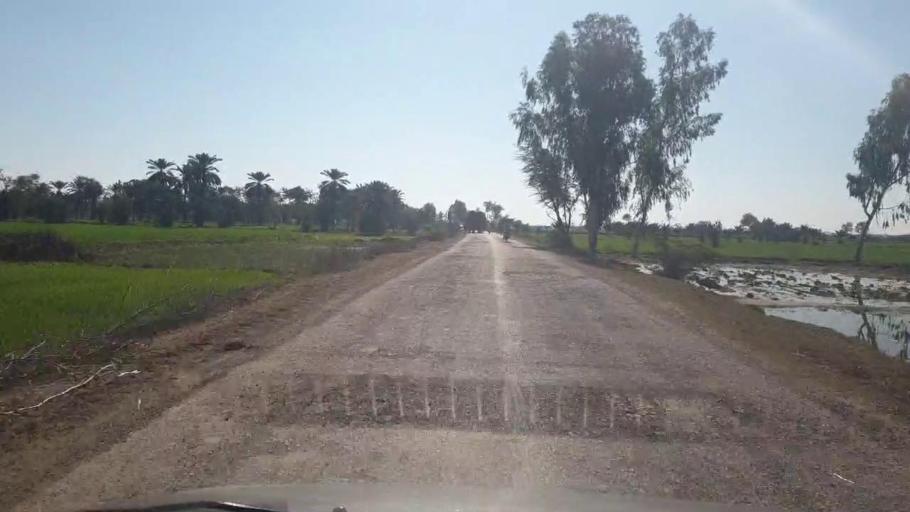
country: PK
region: Sindh
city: Bozdar
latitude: 27.1673
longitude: 68.6432
